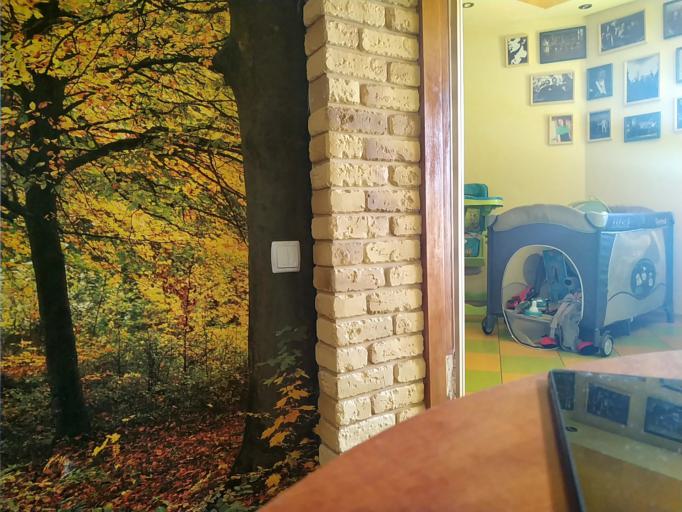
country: RU
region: Tverskaya
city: Vyshniy Volochek
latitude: 57.5331
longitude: 34.6104
